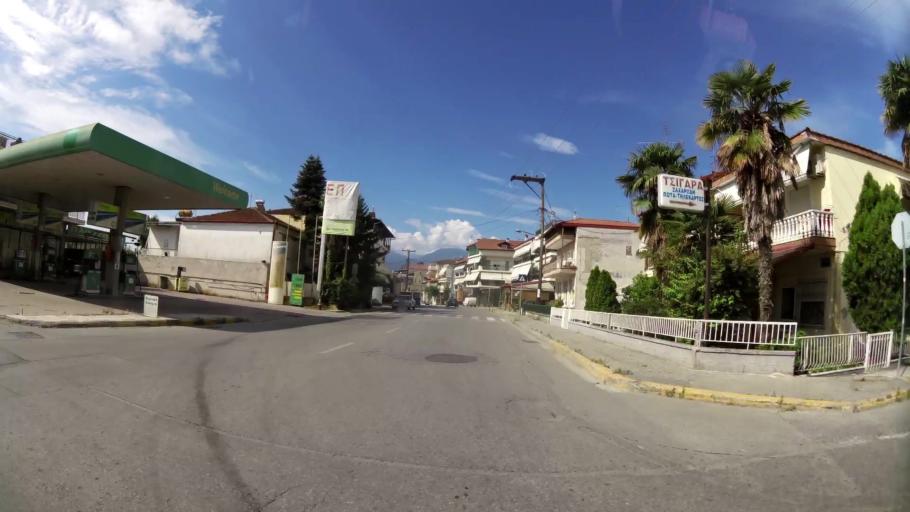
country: GR
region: Central Macedonia
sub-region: Nomos Pierias
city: Katerini
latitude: 40.2764
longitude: 22.5142
